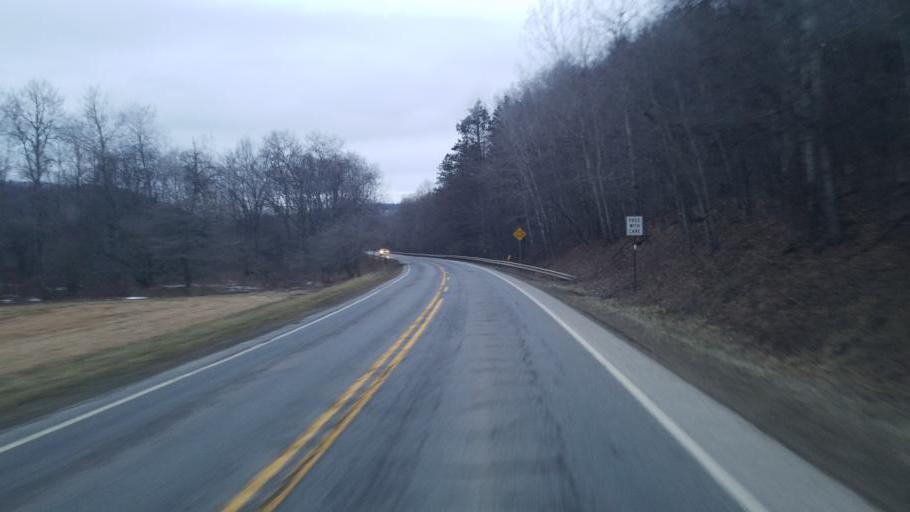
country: US
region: Pennsylvania
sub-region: Potter County
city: Coudersport
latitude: 41.8359
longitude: -77.9214
